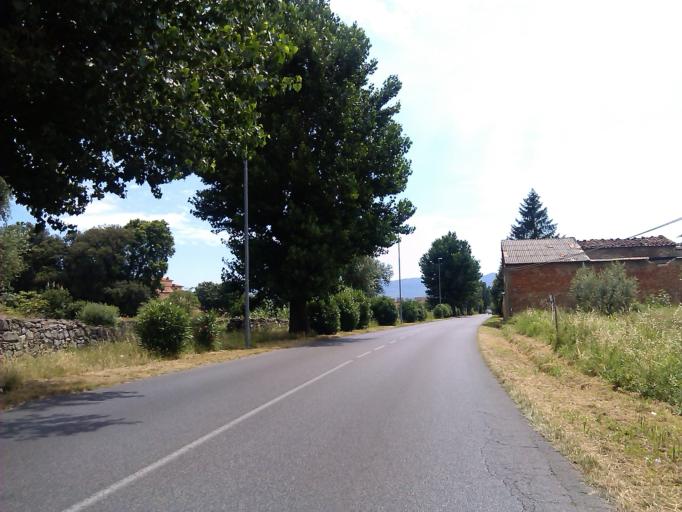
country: IT
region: Tuscany
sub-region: Provincia di Pistoia
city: Montale
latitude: 43.9403
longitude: 11.0288
